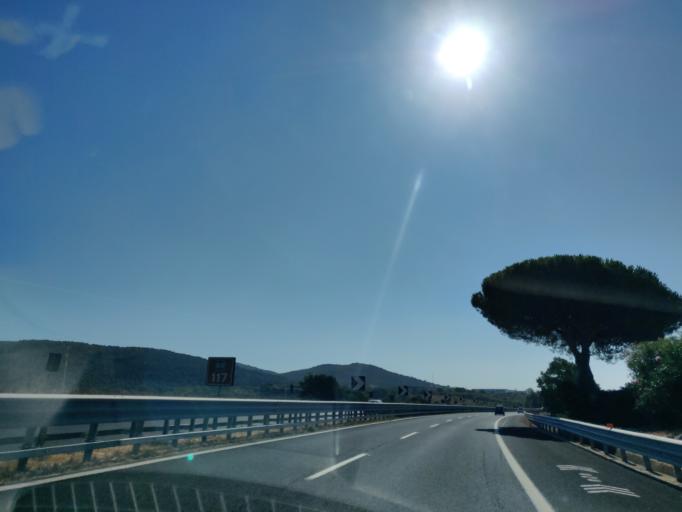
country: IT
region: Latium
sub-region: Citta metropolitana di Roma Capitale
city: Santa Marinella
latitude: 42.0435
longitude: 11.9257
